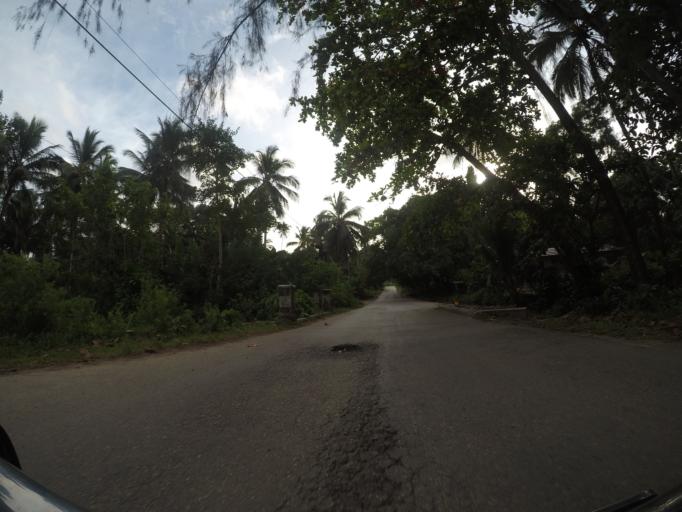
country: TZ
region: Pemba South
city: Chake Chake
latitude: -5.2757
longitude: 39.7705
